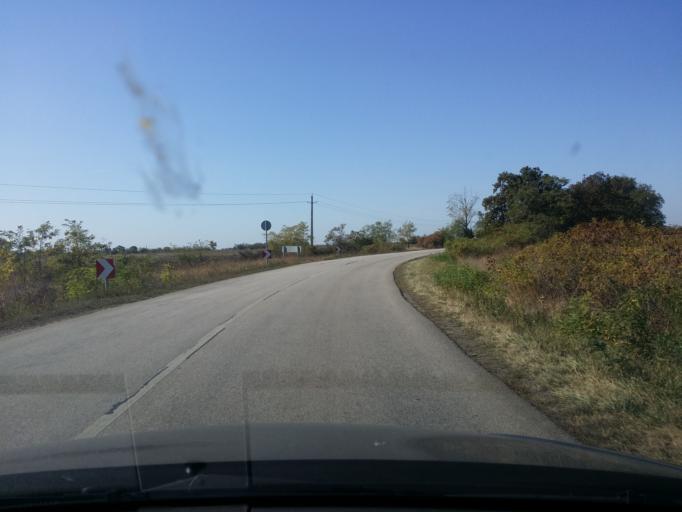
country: HU
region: Jasz-Nagykun-Szolnok
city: Mezotur
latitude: 46.9978
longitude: 20.5680
